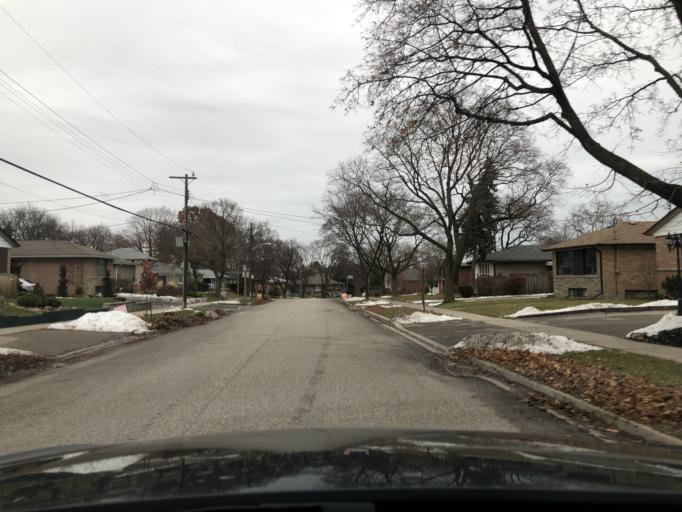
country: CA
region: Ontario
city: Etobicoke
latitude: 43.6949
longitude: -79.5374
